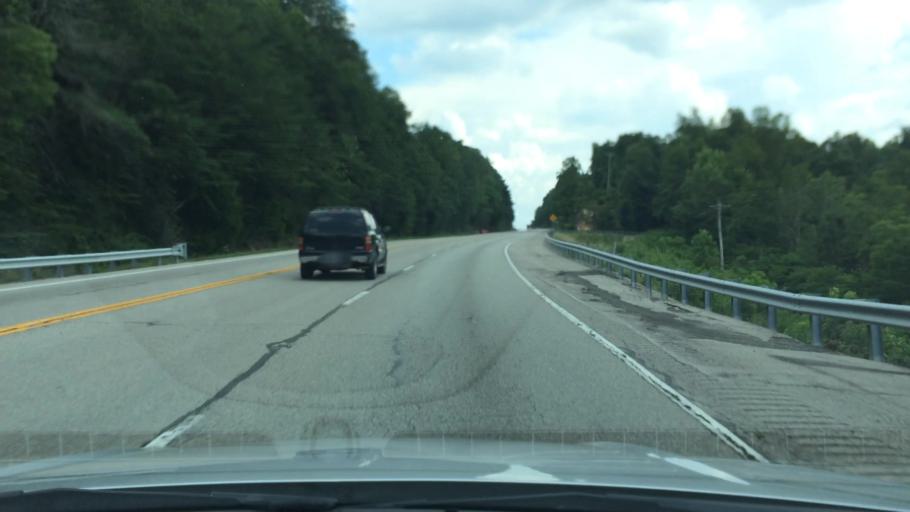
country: US
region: Kentucky
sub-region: Pulaski County
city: Somerset
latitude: 36.9335
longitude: -84.5248
